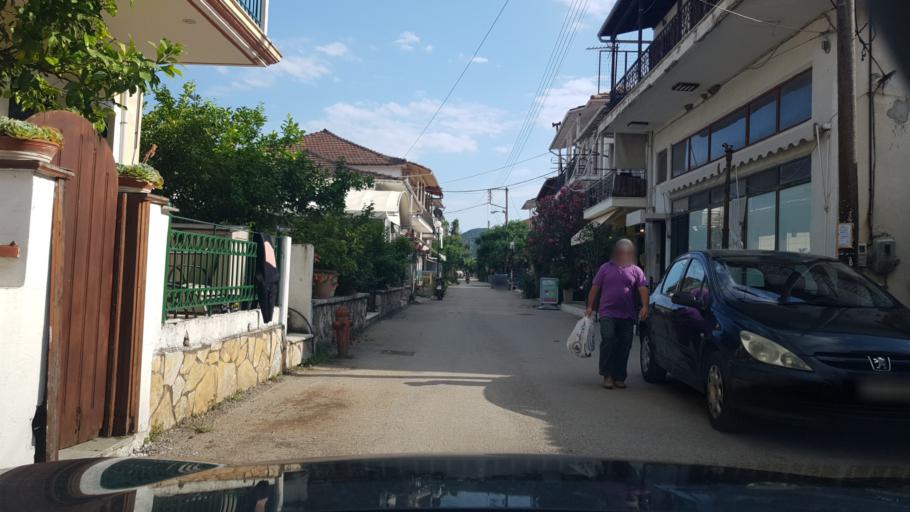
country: GR
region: Ionian Islands
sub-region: Lefkada
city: Nidri
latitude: 38.6860
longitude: 20.6983
